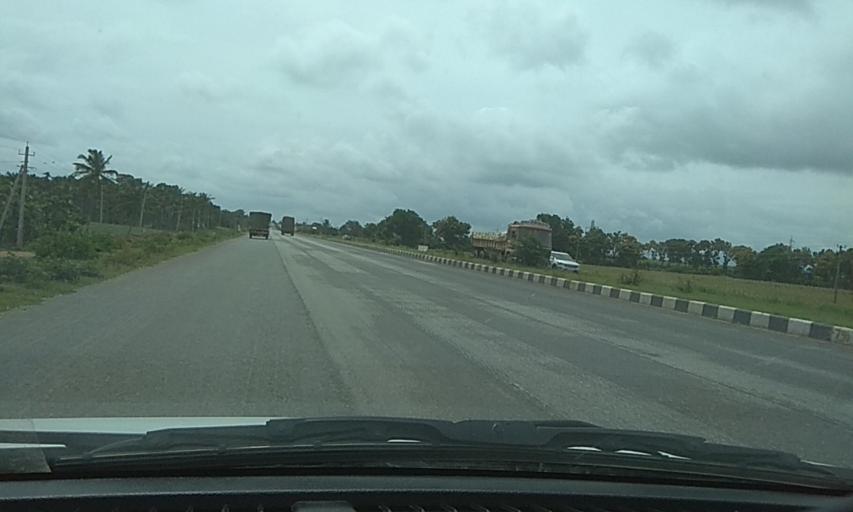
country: IN
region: Karnataka
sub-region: Davanagere
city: Mayakonda
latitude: 14.3348
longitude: 76.2152
